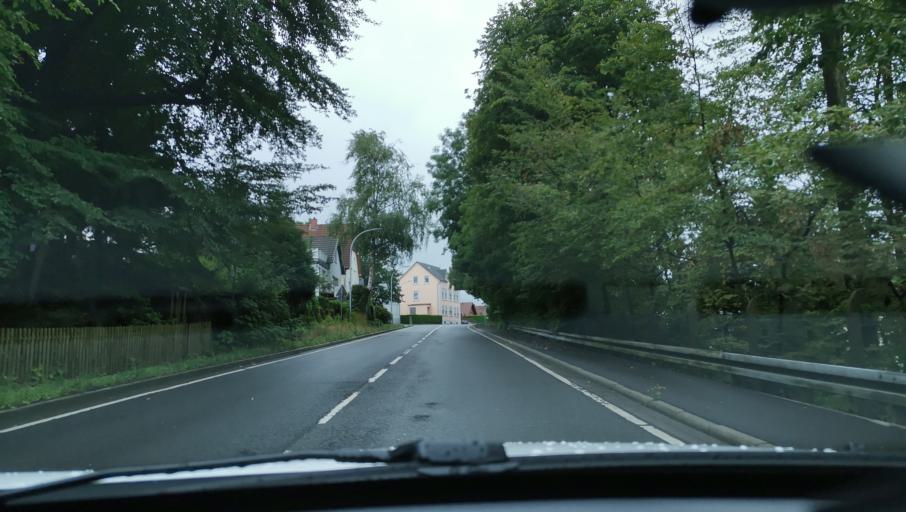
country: DE
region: North Rhine-Westphalia
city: Halver
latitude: 51.1948
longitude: 7.5102
